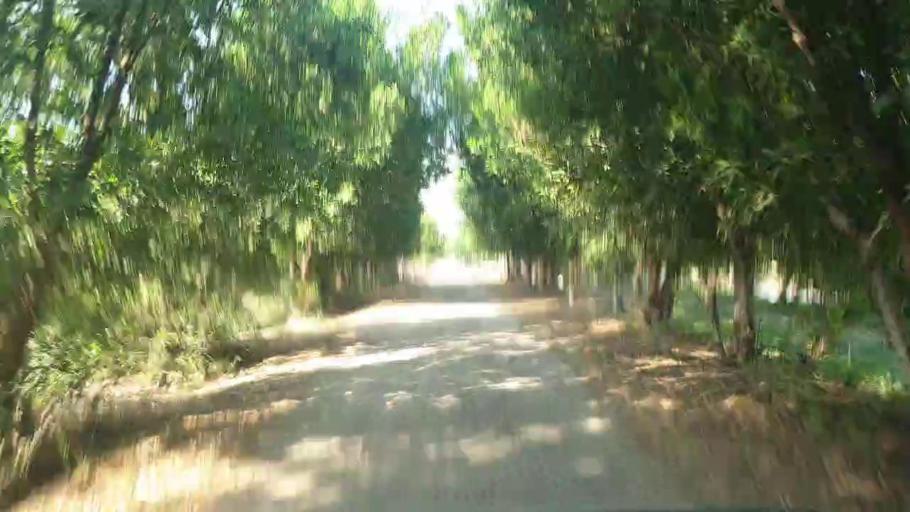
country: PK
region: Sindh
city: Badin
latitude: 24.6258
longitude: 68.8148
